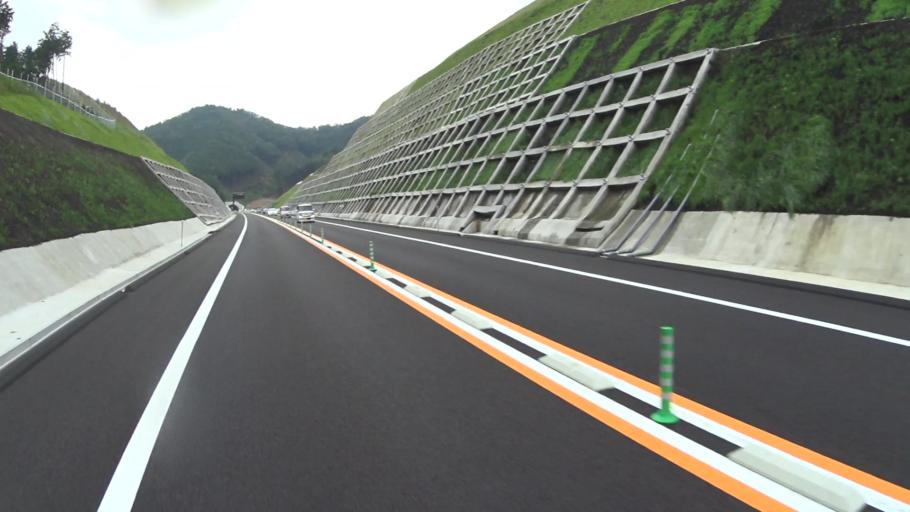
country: JP
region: Kyoto
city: Ayabe
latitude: 35.2148
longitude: 135.3432
